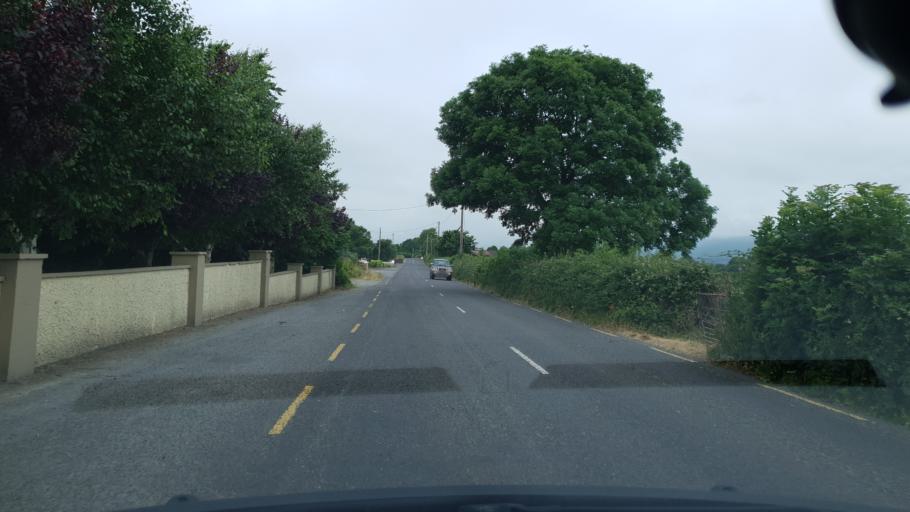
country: IE
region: Munster
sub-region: Ciarrai
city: Tralee
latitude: 52.1636
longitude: -9.6305
